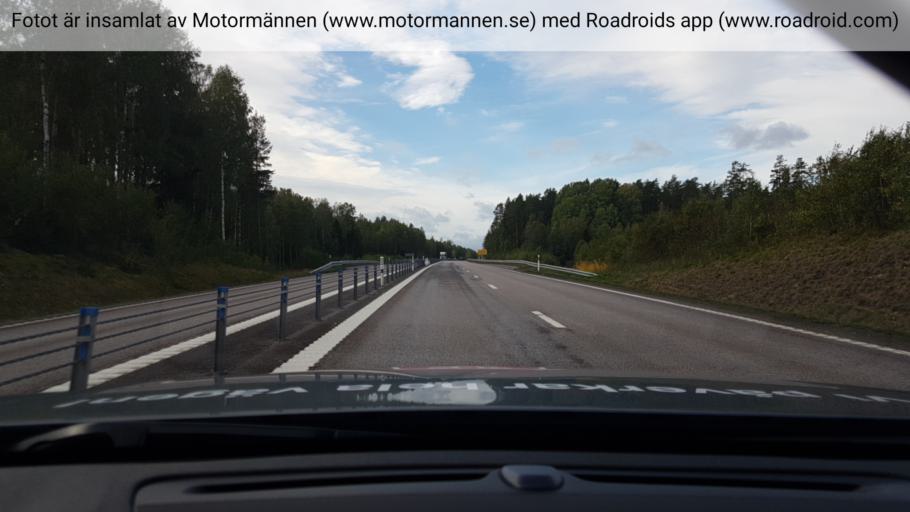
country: SE
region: Vaermland
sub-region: Karlstads Kommun
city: Edsvalla
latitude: 59.3888
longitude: 13.2563
